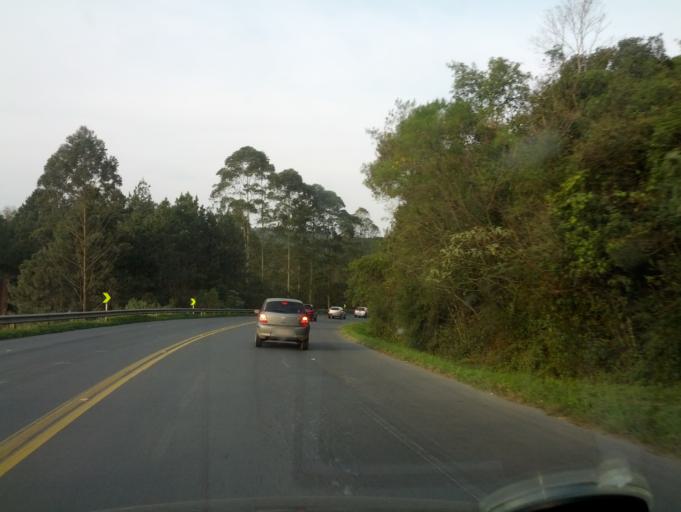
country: BR
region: Santa Catarina
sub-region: Otacilio Costa
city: Otacilio Costa
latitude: -27.2830
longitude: -50.0757
